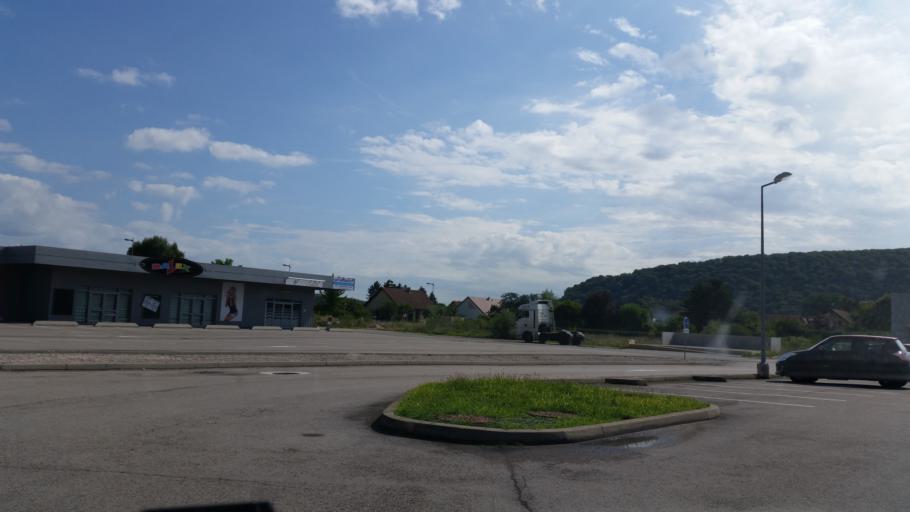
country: FR
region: Franche-Comte
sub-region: Departement du Doubs
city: Mathay
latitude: 47.4408
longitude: 6.7786
